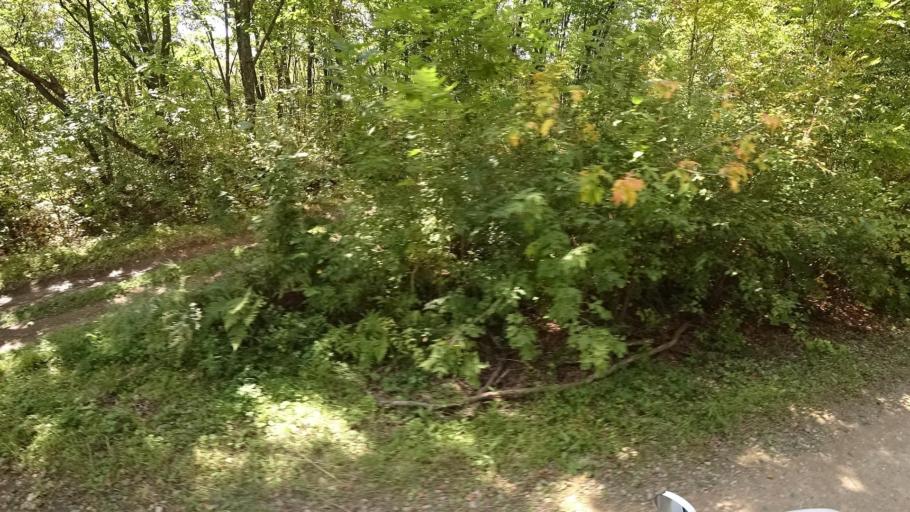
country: RU
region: Primorskiy
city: Kirovskiy
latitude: 44.7599
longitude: 133.6222
